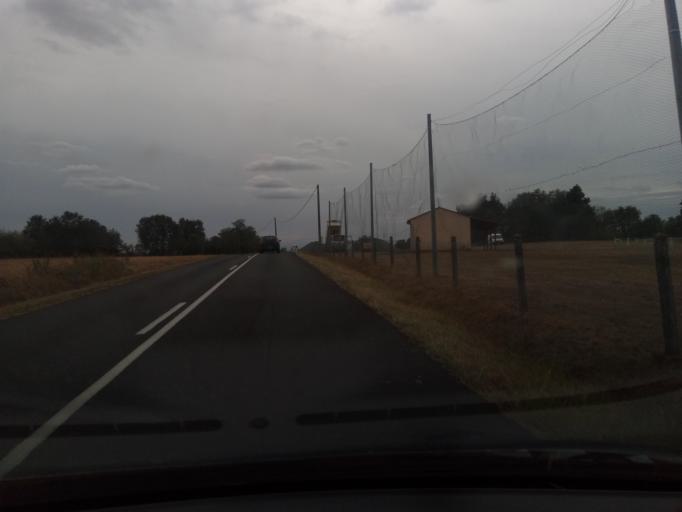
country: FR
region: Poitou-Charentes
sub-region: Departement de la Vienne
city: Pleumartin
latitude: 46.6461
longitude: 0.7608
